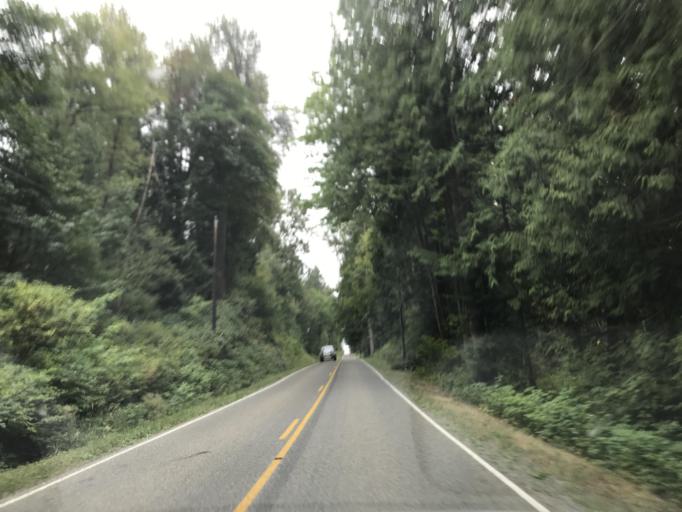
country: US
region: Washington
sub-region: Whatcom County
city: Sudden Valley
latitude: 48.7869
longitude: -122.3331
